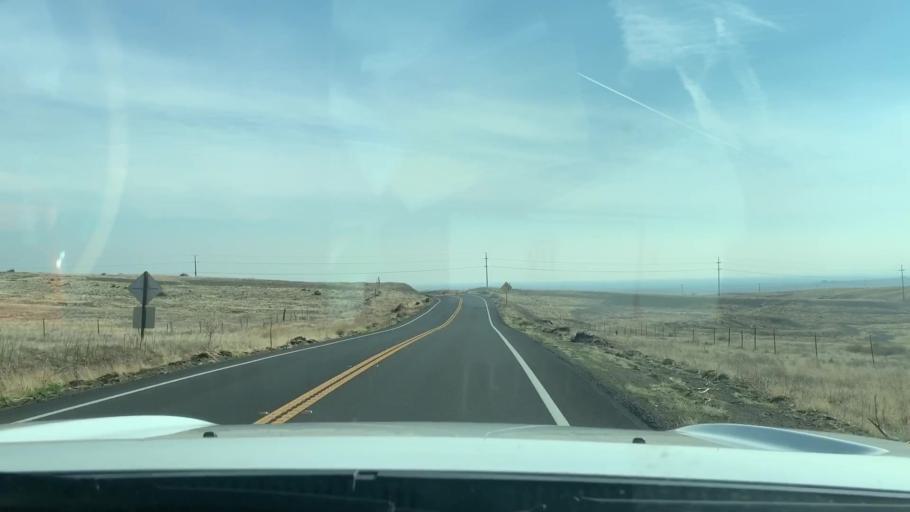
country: US
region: California
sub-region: Fresno County
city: Coalinga
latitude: 36.2488
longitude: -120.3041
